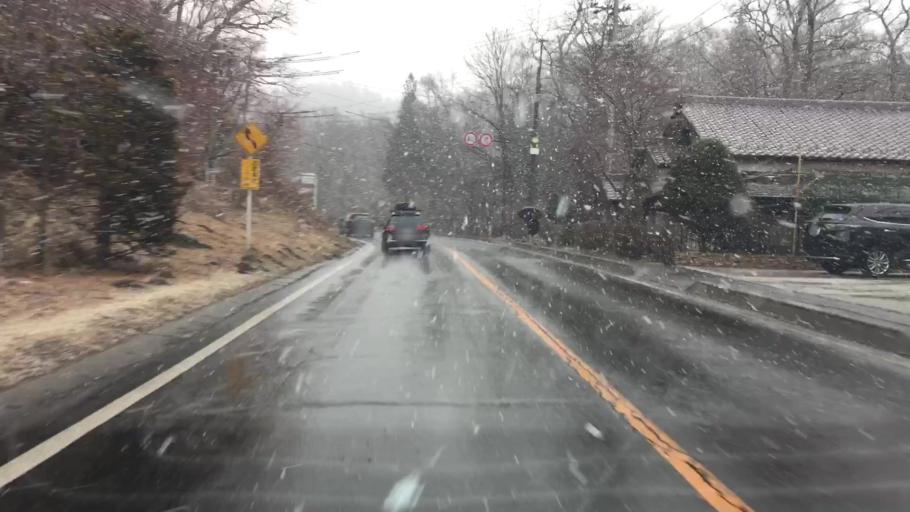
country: JP
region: Nagano
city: Komoro
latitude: 36.3567
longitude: 138.5900
